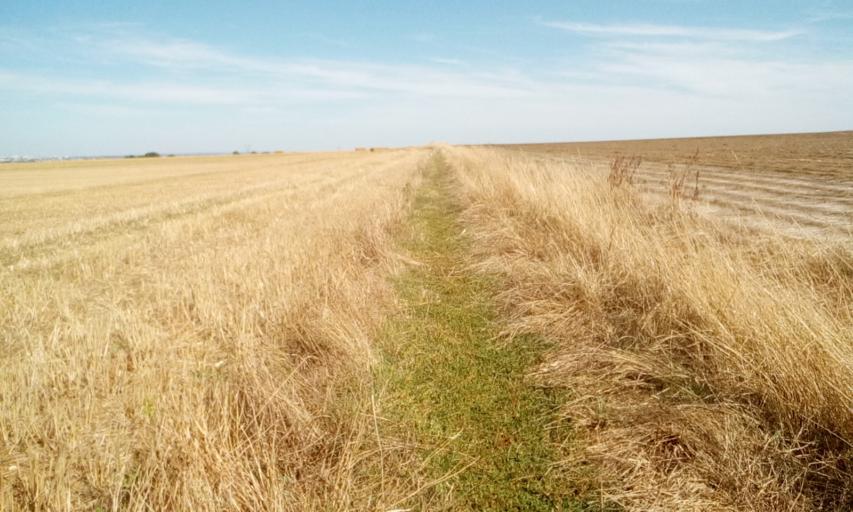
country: FR
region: Lower Normandy
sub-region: Departement du Calvados
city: Fontaine-Etoupefour
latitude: 49.1289
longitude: -0.4611
